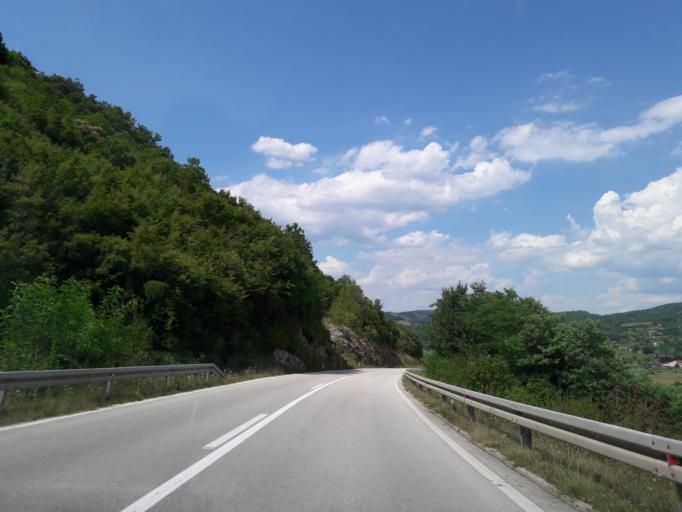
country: BA
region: Republika Srpska
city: Mrkonjic Grad
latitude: 44.5215
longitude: 17.1508
